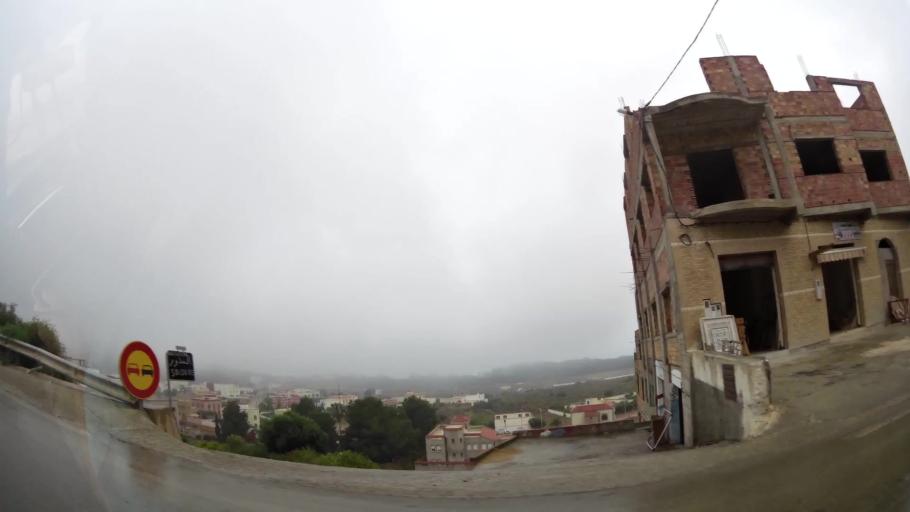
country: MA
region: Taza-Al Hoceima-Taounate
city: Imzourene
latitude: 35.1979
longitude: -3.8999
